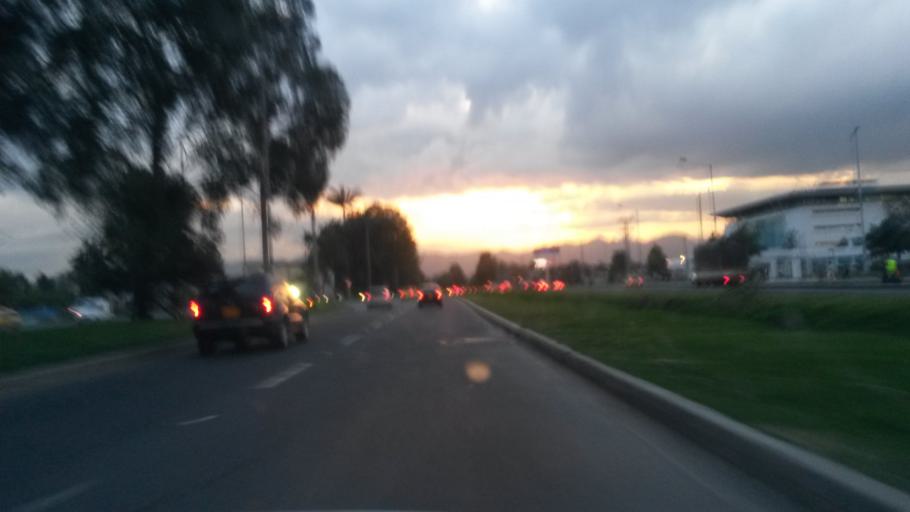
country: CO
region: Cundinamarca
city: Funza
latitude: 4.6921
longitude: -74.1346
